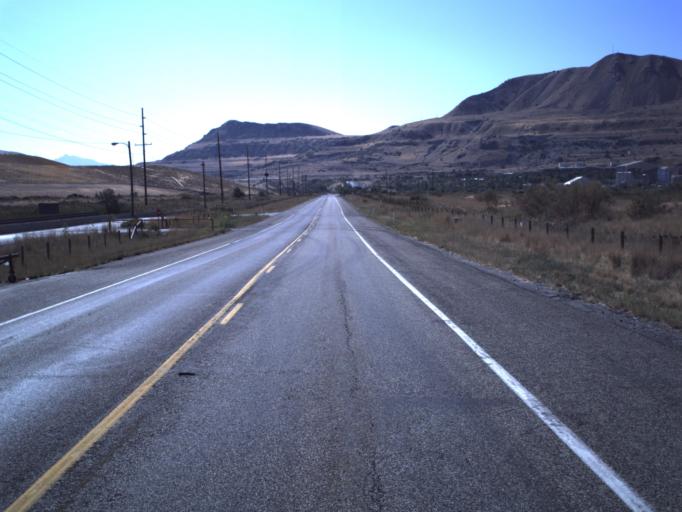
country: US
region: Utah
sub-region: Salt Lake County
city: Magna
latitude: 40.7387
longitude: -112.1753
